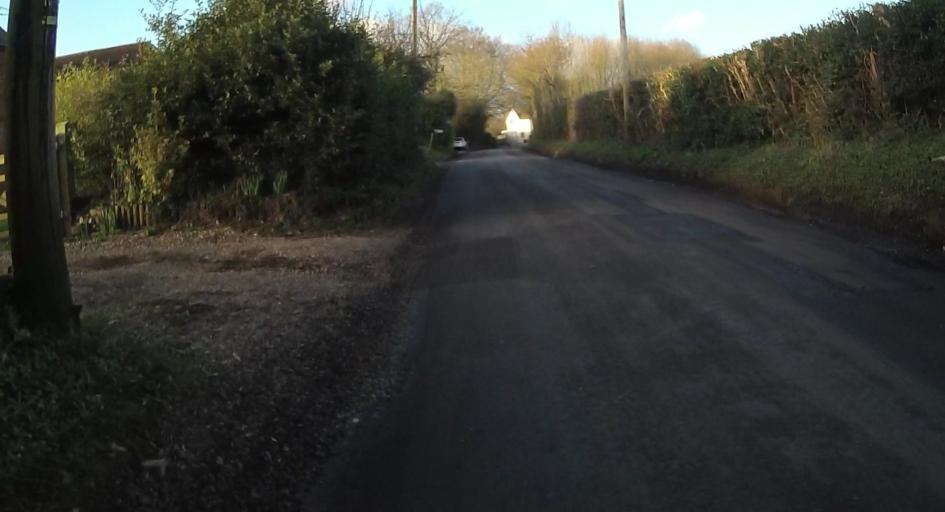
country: GB
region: England
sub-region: Hampshire
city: Four Marks
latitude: 51.1240
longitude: -1.0633
